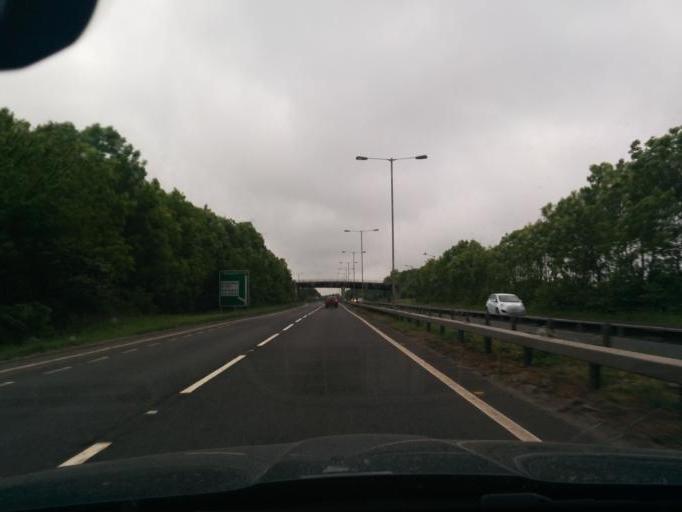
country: GB
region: England
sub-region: Northumberland
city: Ashington
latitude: 55.1437
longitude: -1.5546
